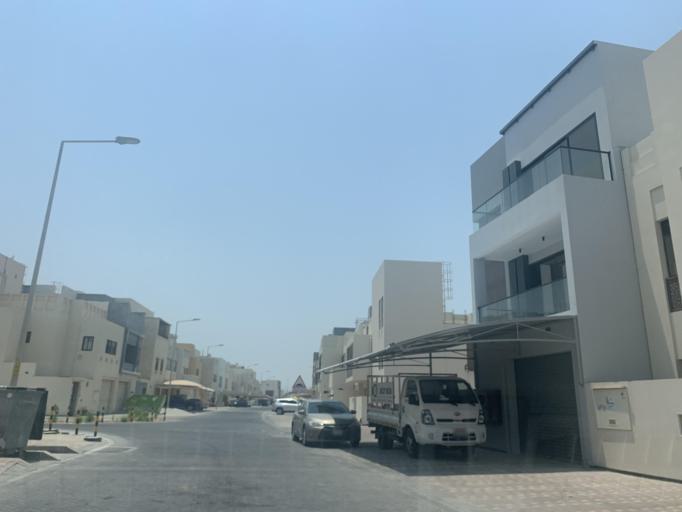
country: BH
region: Muharraq
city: Al Hadd
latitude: 26.2362
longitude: 50.6757
